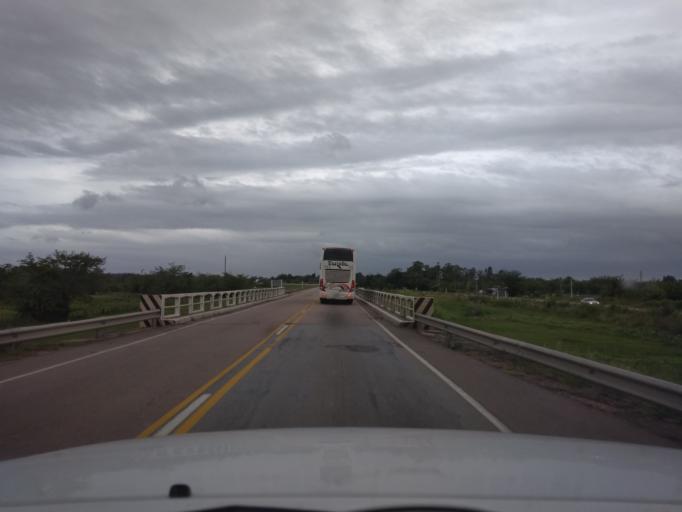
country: UY
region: Canelones
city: Canelones
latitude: -34.5025
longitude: -56.2816
